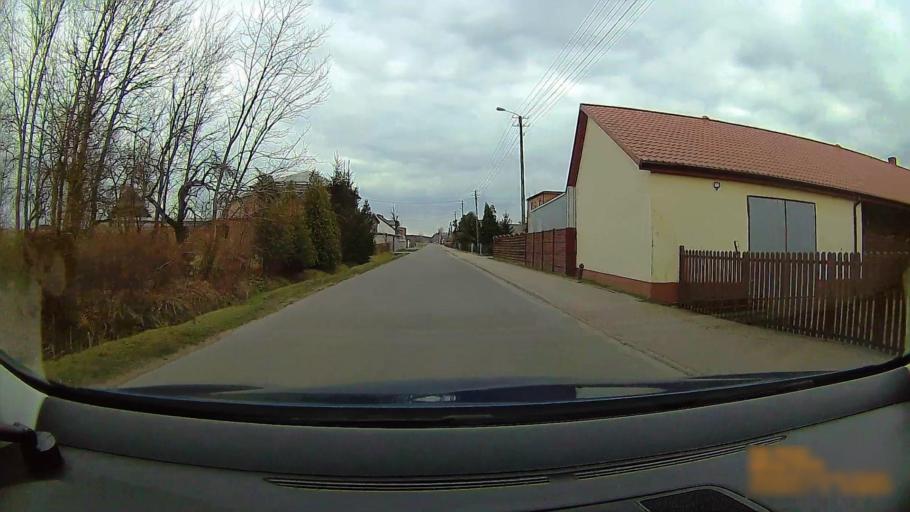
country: PL
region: Greater Poland Voivodeship
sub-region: Powiat koninski
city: Rychwal
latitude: 52.0948
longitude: 18.1405
